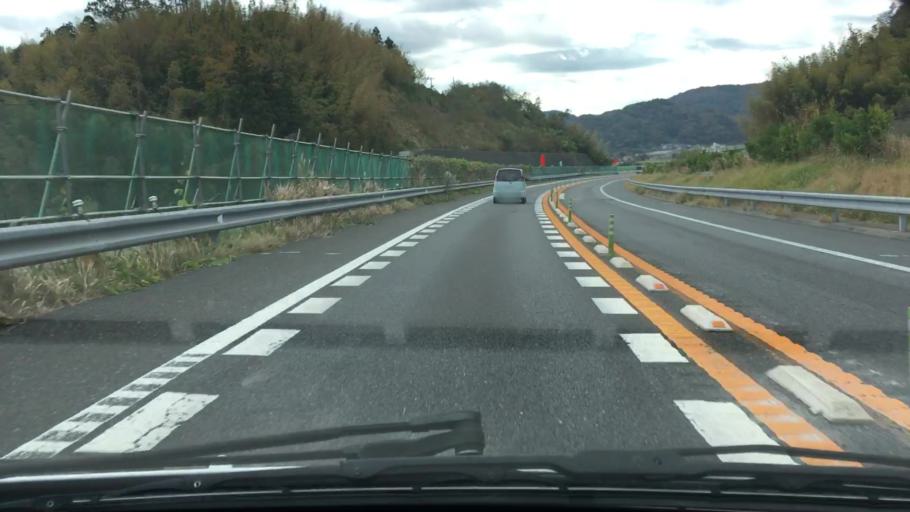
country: JP
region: Chiba
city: Kimitsu
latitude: 35.2286
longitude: 139.8867
